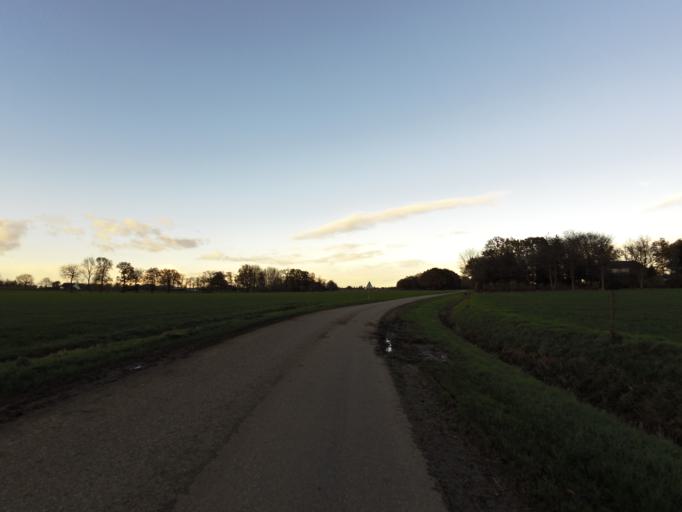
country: NL
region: Gelderland
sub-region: Oude IJsselstreek
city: Gendringen
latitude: 51.8574
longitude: 6.3565
